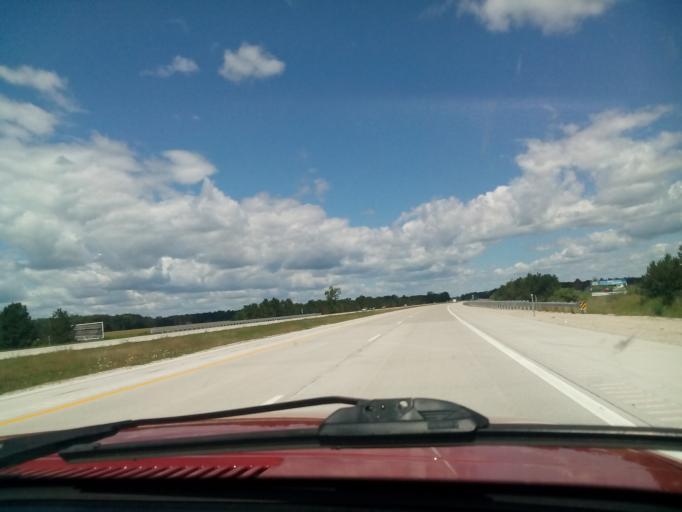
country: US
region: Michigan
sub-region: Bay County
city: Pinconning
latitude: 43.8744
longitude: -84.0221
